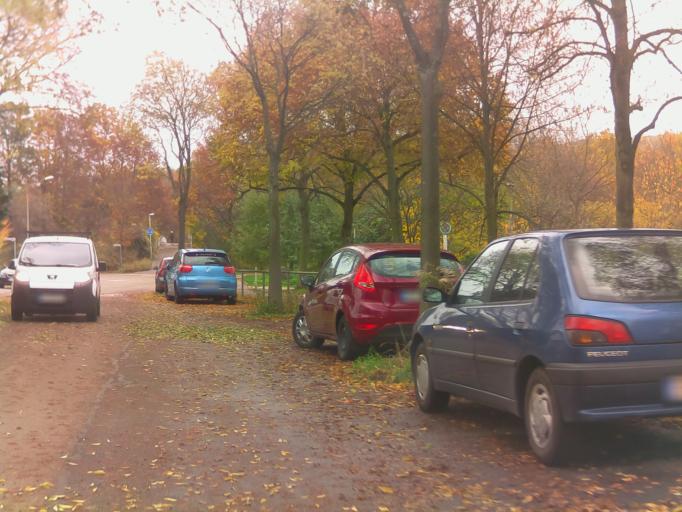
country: DE
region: Baden-Wuerttemberg
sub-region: Karlsruhe Region
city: Weinheim
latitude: 49.5430
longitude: 8.6530
